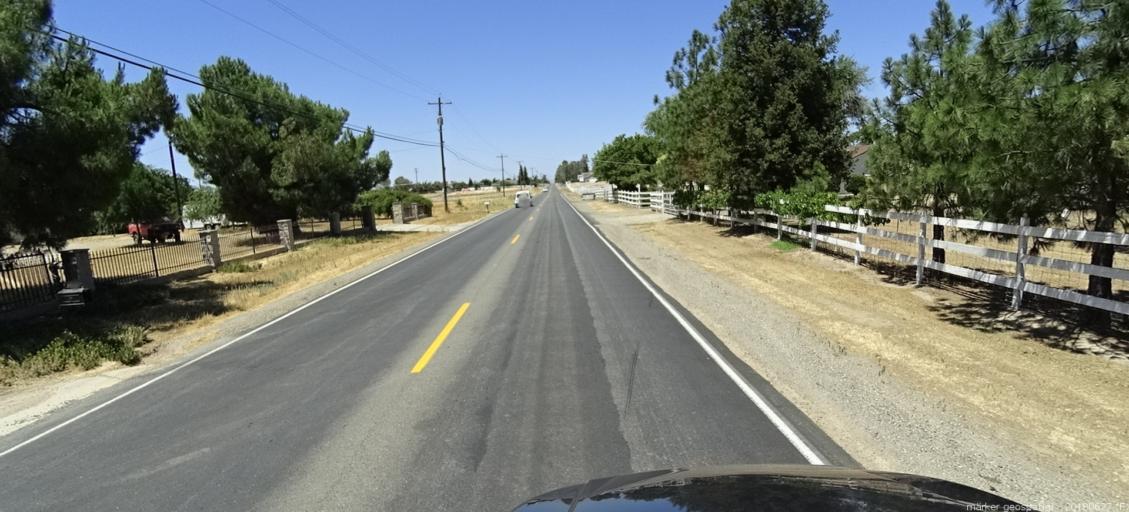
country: US
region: California
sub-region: Madera County
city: Bonadelle Ranchos-Madera Ranchos
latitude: 36.9394
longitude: -119.9122
